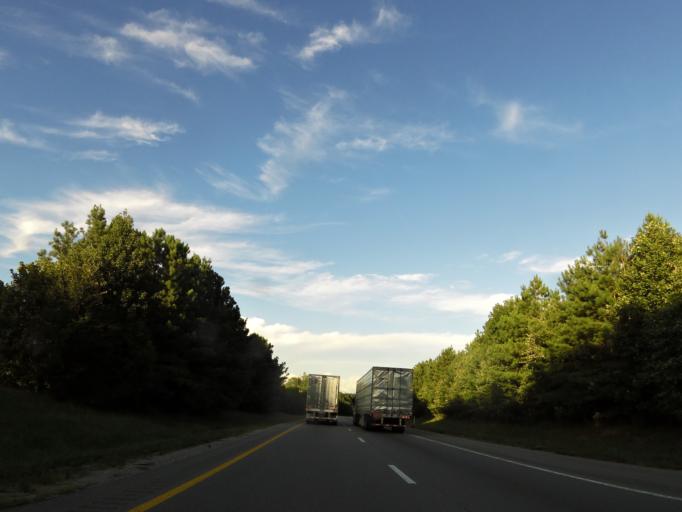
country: US
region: Tennessee
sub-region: Putnam County
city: Baxter
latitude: 36.1345
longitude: -85.6489
